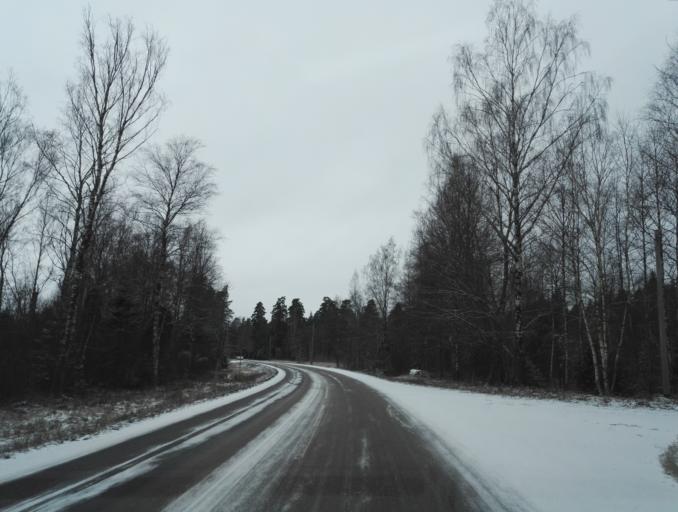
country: SE
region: Kronoberg
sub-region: Lessebo Kommun
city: Hovmantorp
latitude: 56.6670
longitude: 15.1535
